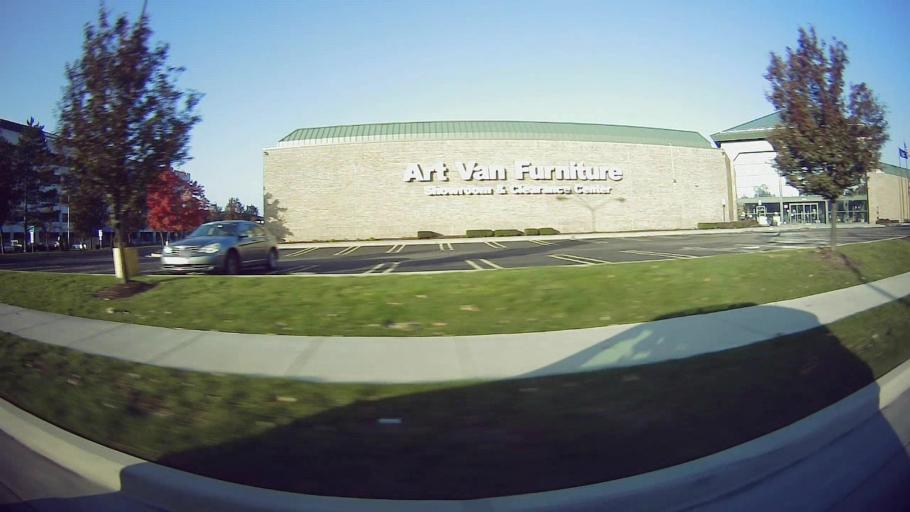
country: US
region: Michigan
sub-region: Oakland County
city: Oak Park
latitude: 42.4582
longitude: -83.2013
